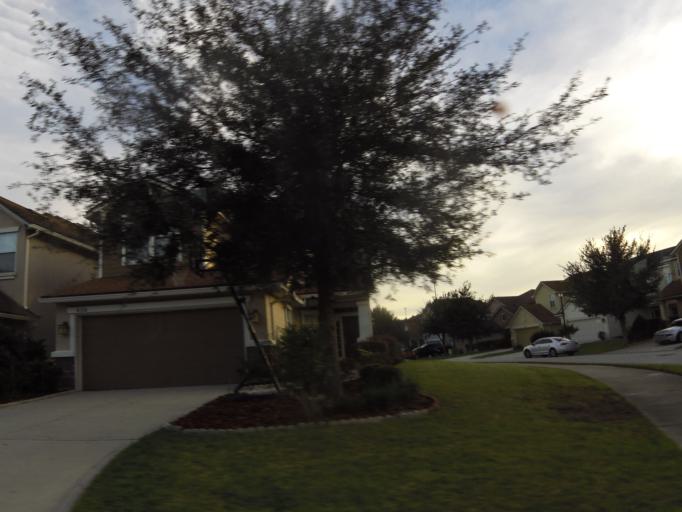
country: US
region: Florida
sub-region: Saint Johns County
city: Fruit Cove
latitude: 30.1612
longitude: -81.5502
